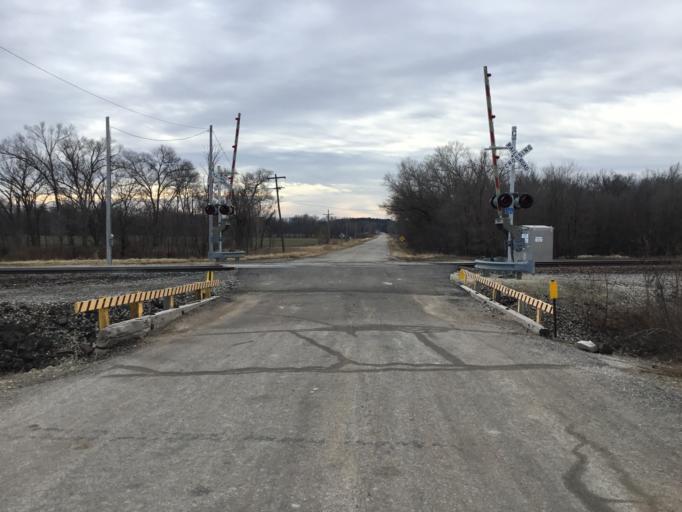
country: US
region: Kansas
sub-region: Marion County
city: Marion
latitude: 38.2688
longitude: -96.8194
